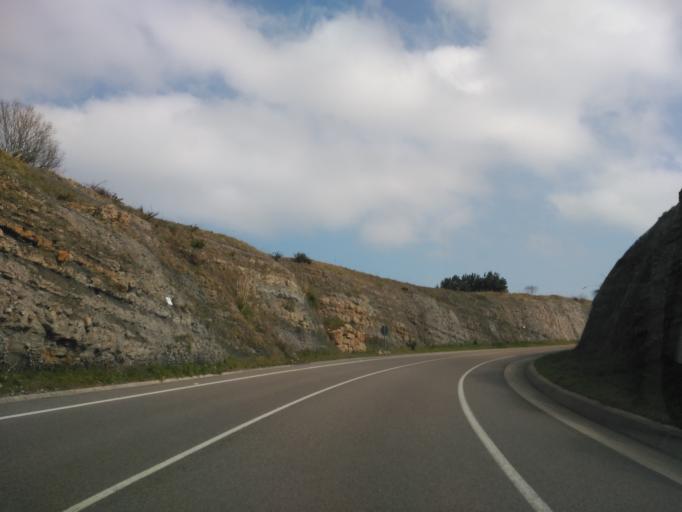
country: ES
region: Cantabria
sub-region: Provincia de Cantabria
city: Santillana
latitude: 43.3835
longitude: -4.1005
